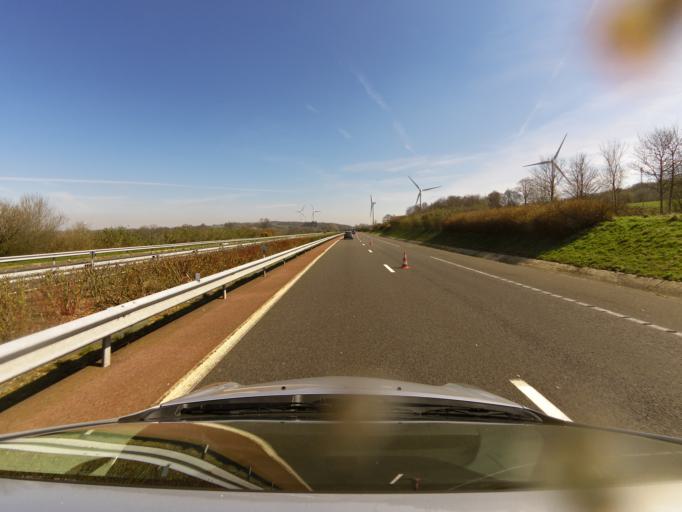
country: FR
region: Lower Normandy
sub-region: Departement de la Manche
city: Percy
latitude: 48.8943
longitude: -1.1265
